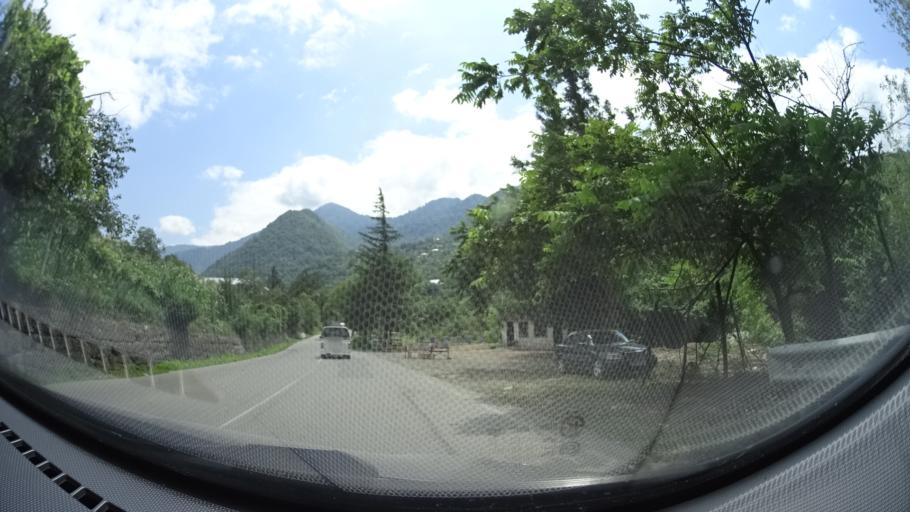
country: TR
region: Artvin
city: Camili
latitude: 41.5658
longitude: 41.8300
